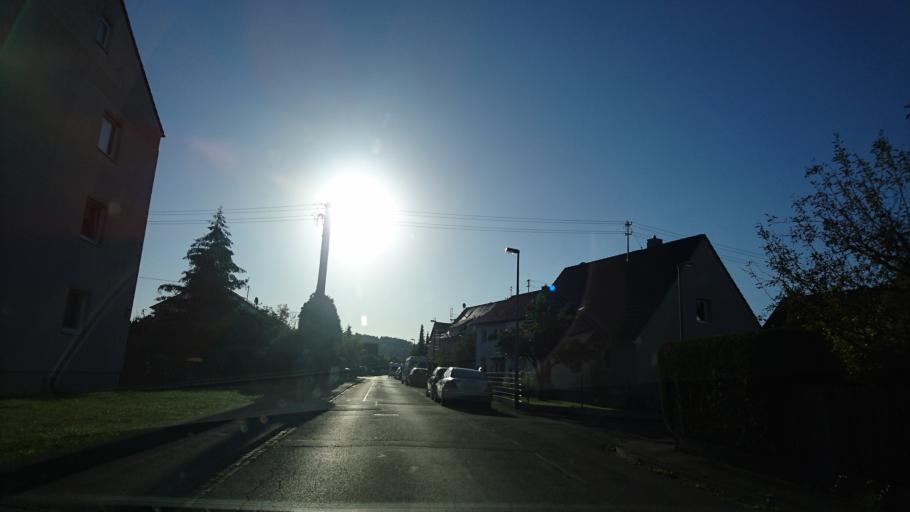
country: DE
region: Bavaria
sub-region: Swabia
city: Gersthofen
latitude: 48.4226
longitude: 10.8834
